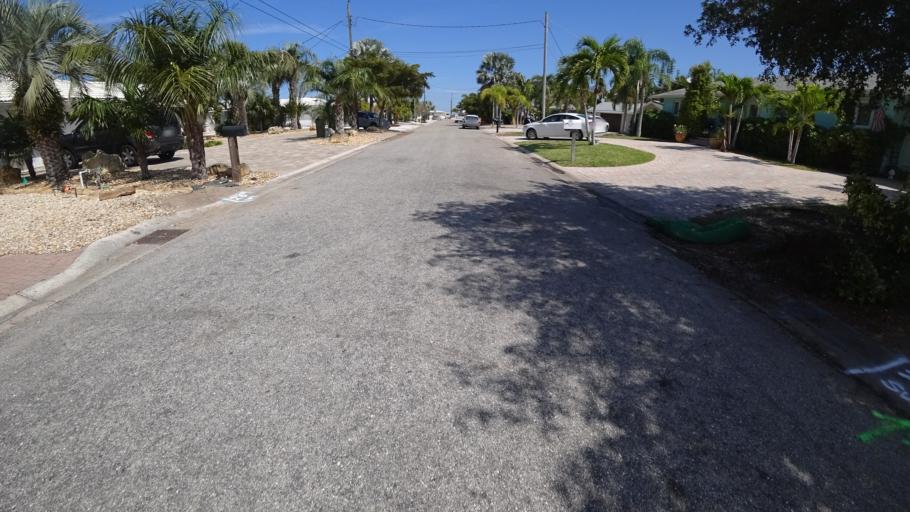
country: US
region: Florida
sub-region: Manatee County
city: Cortez
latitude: 27.4680
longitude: -82.6617
